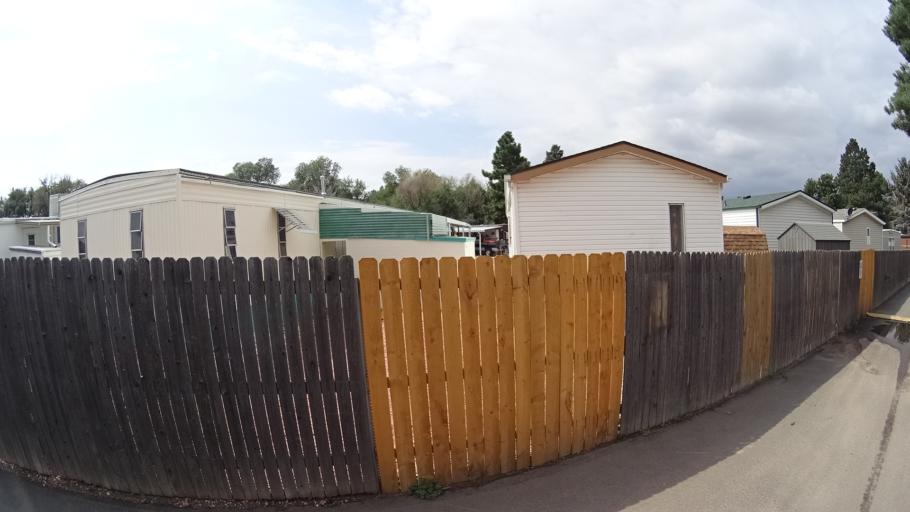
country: US
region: Colorado
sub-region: El Paso County
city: Colorado Springs
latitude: 38.8831
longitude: -104.8244
